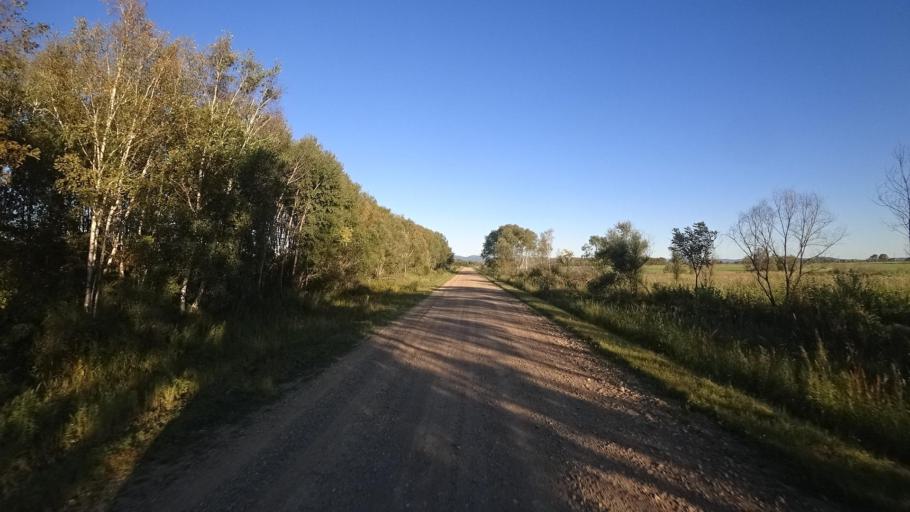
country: RU
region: Primorskiy
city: Kirovskiy
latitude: 44.8247
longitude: 133.5989
